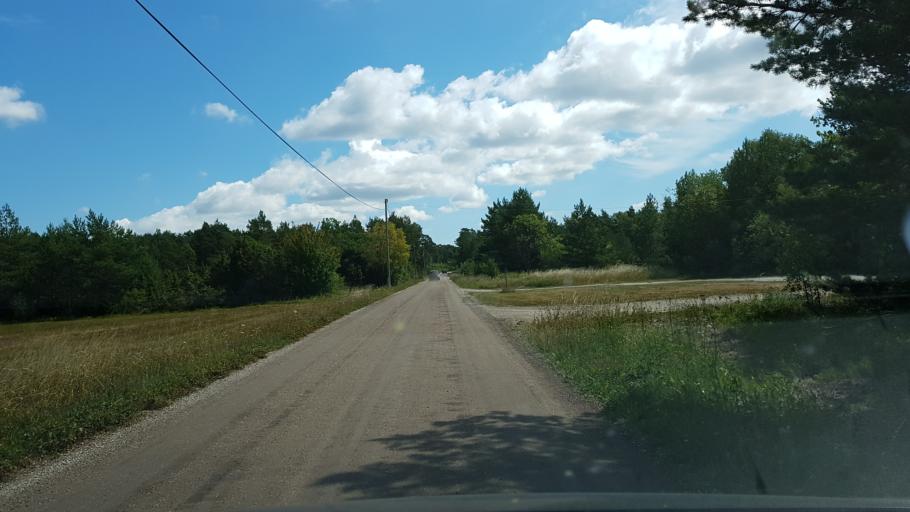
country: SE
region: Gotland
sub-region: Gotland
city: Visby
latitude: 57.8033
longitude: 18.5017
